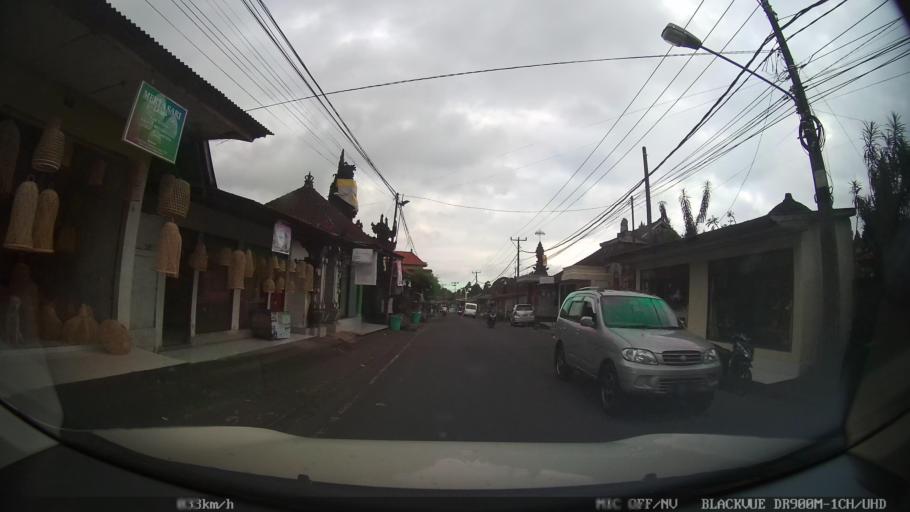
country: ID
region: Bali
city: Banjar Ubud
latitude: -8.4690
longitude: 115.2771
